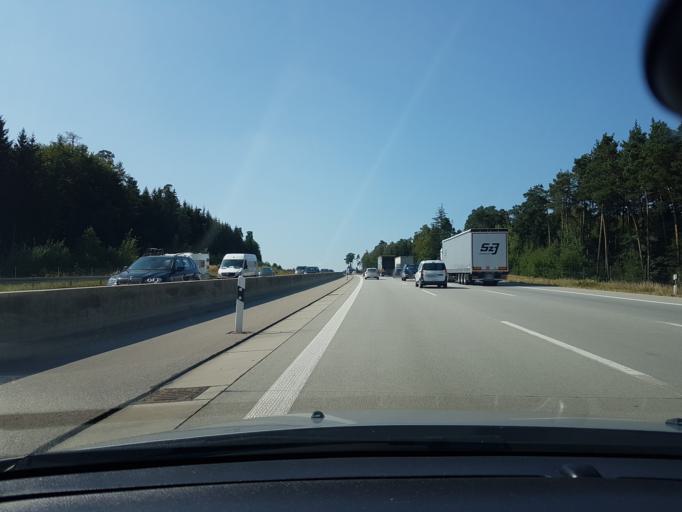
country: DE
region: Bavaria
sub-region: Swabia
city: Adelzhausen
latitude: 48.3372
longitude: 11.1593
